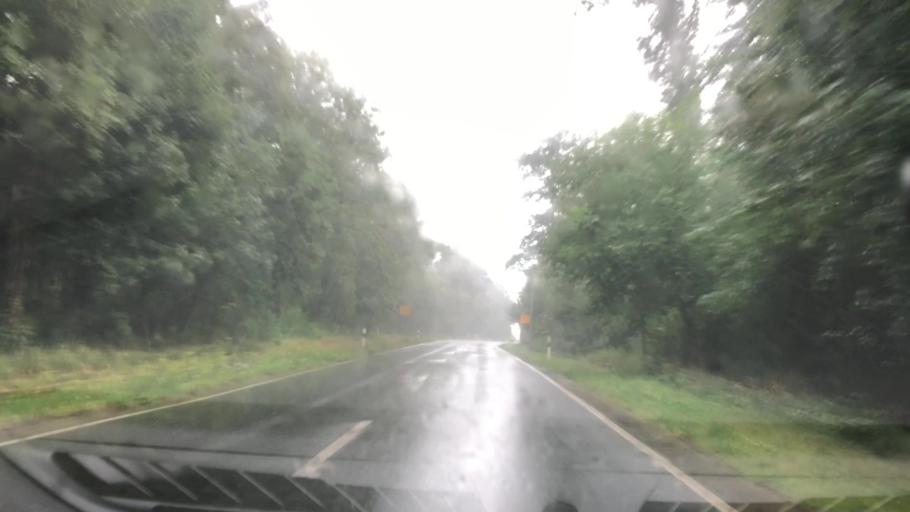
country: DE
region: Lower Saxony
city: Buckeburg
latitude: 52.2649
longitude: 8.9878
